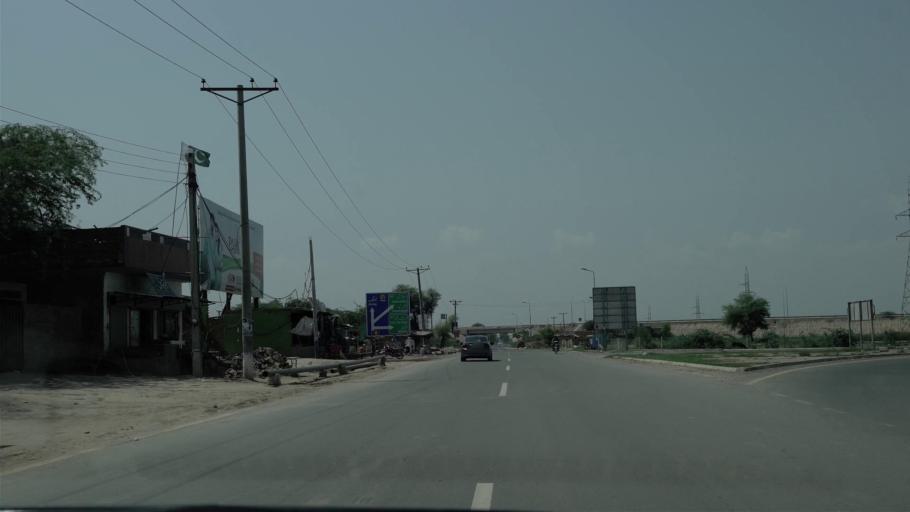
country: PK
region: Punjab
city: Gojra
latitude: 31.1779
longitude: 72.6324
